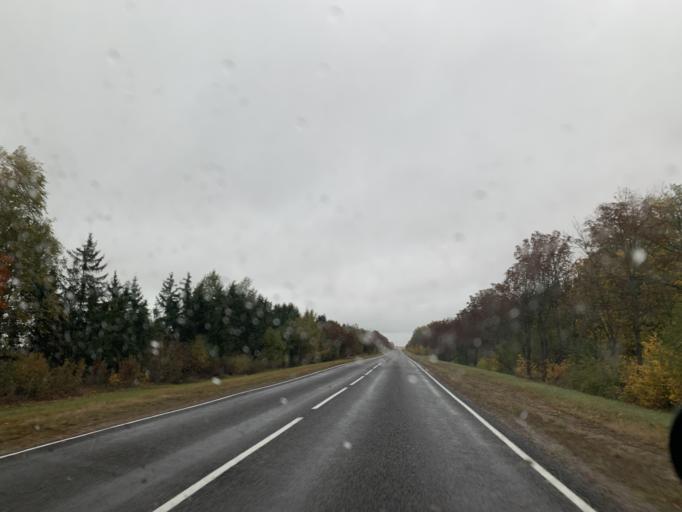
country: BY
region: Minsk
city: Haradzyeya
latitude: 53.3934
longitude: 26.5810
